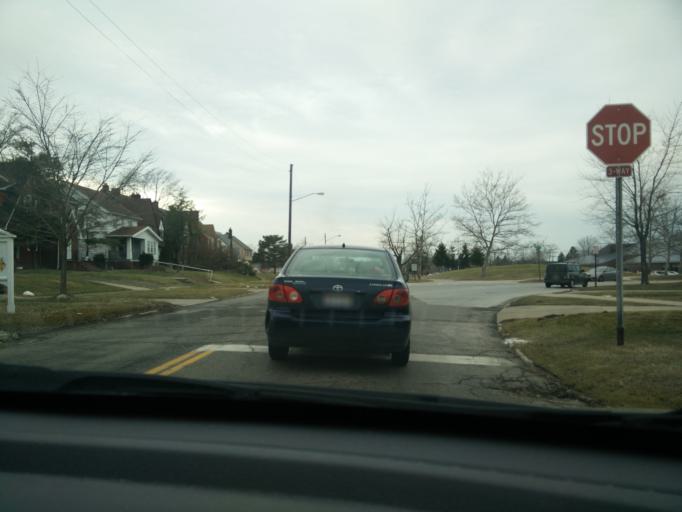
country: US
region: Ohio
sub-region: Cuyahoga County
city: University Heights
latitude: 41.5031
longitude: -81.5531
